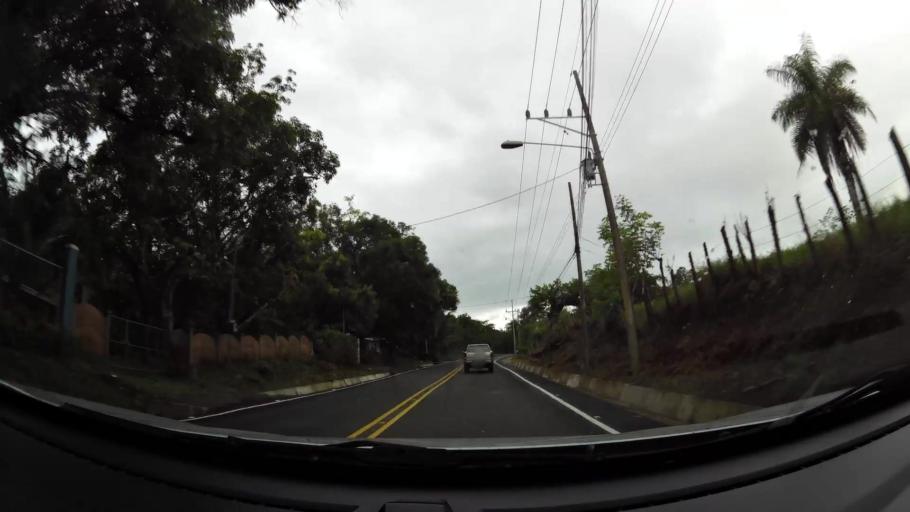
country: CR
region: Alajuela
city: Desamparados
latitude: 9.9378
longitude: -84.5312
